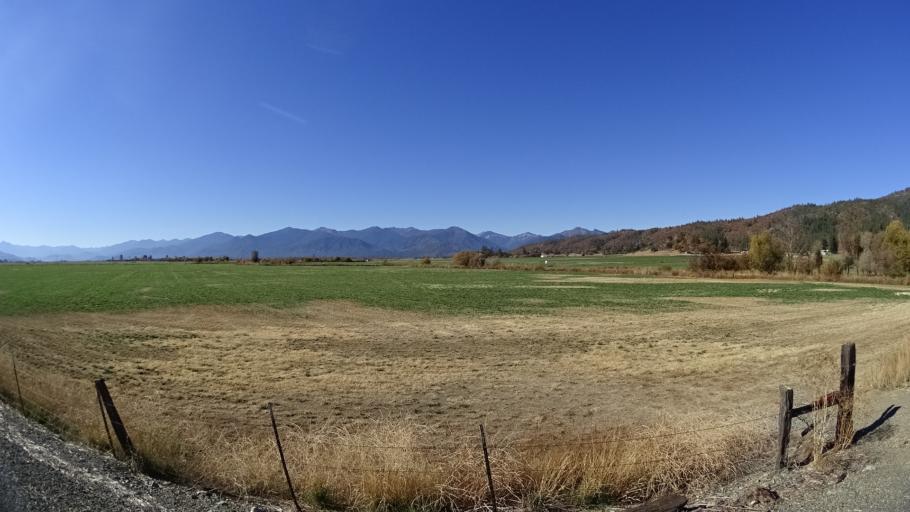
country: US
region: California
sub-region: Siskiyou County
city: Yreka
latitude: 41.5763
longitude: -122.8595
